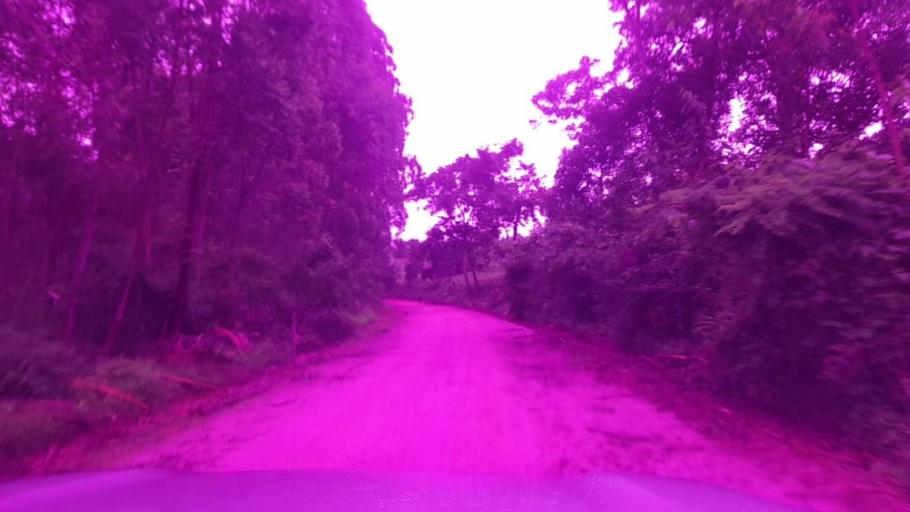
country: ET
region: Southern Nations, Nationalities, and People's Region
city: Bonga
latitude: 7.4602
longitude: 36.1269
